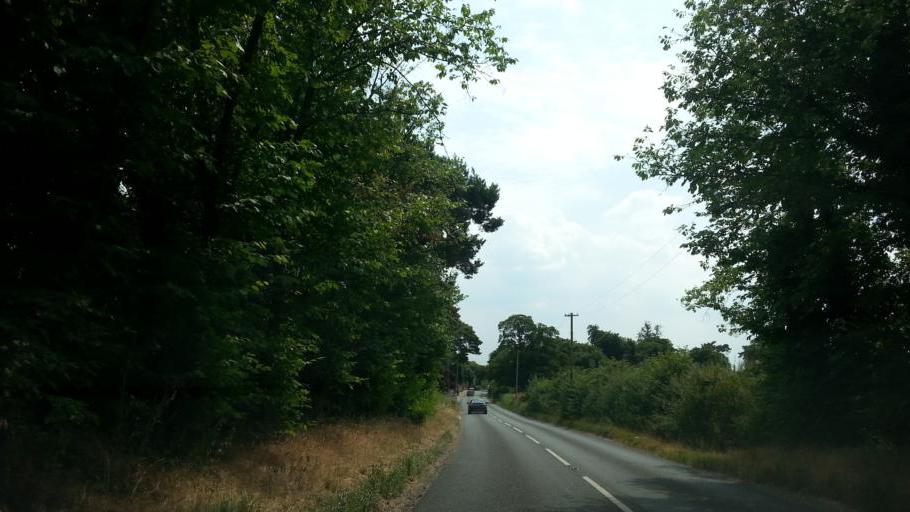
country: GB
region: England
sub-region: Suffolk
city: Lakenheath
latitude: 52.3943
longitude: 0.5289
